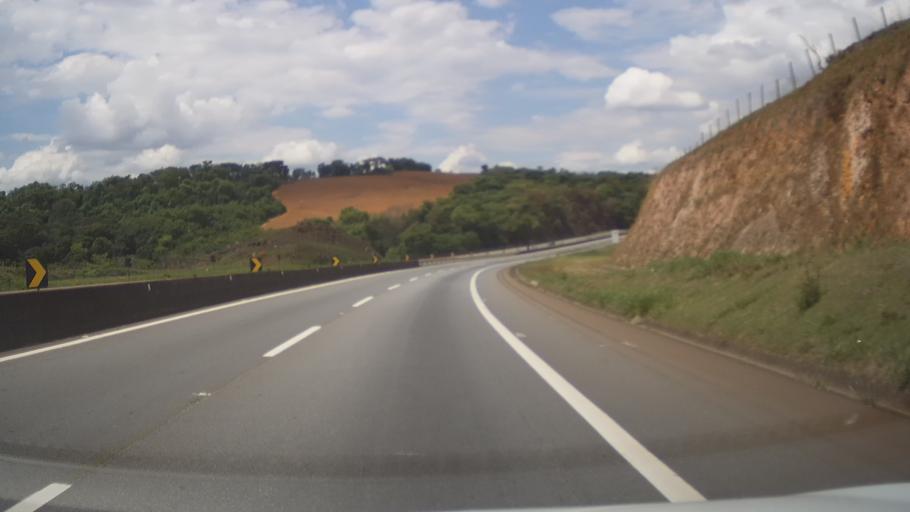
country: BR
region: Minas Gerais
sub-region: Nepomuceno
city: Nepomuceno
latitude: -21.2891
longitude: -45.1468
